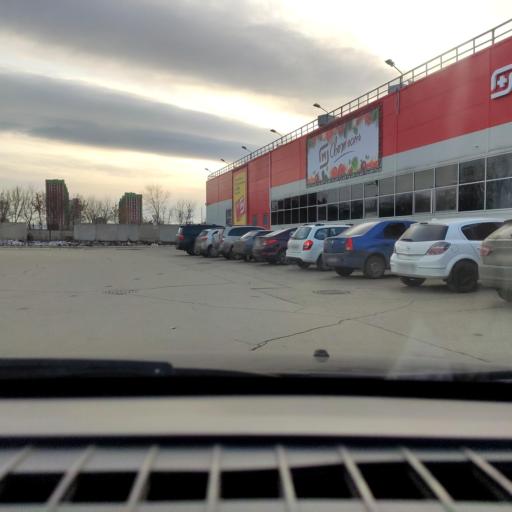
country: RU
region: Samara
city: Tol'yatti
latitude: 53.5237
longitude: 49.2577
